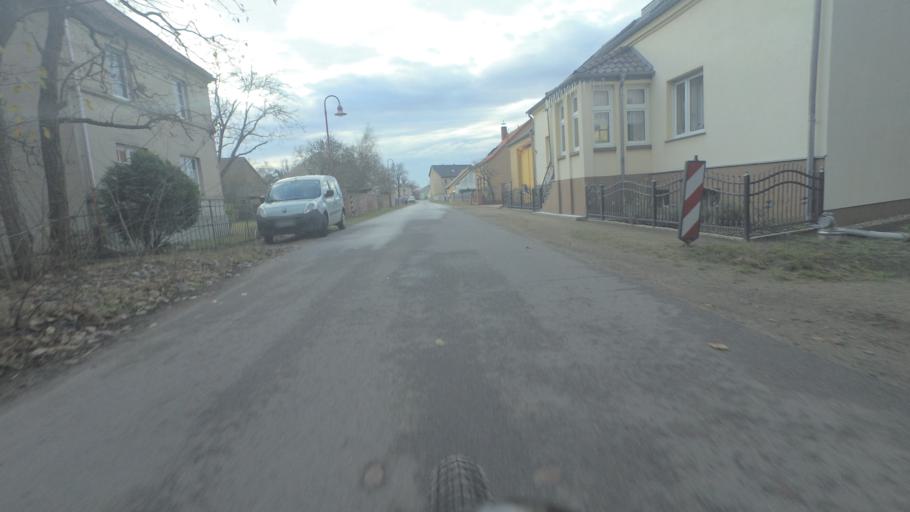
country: DE
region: Brandenburg
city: Am Mellensee
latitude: 52.2298
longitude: 13.3548
